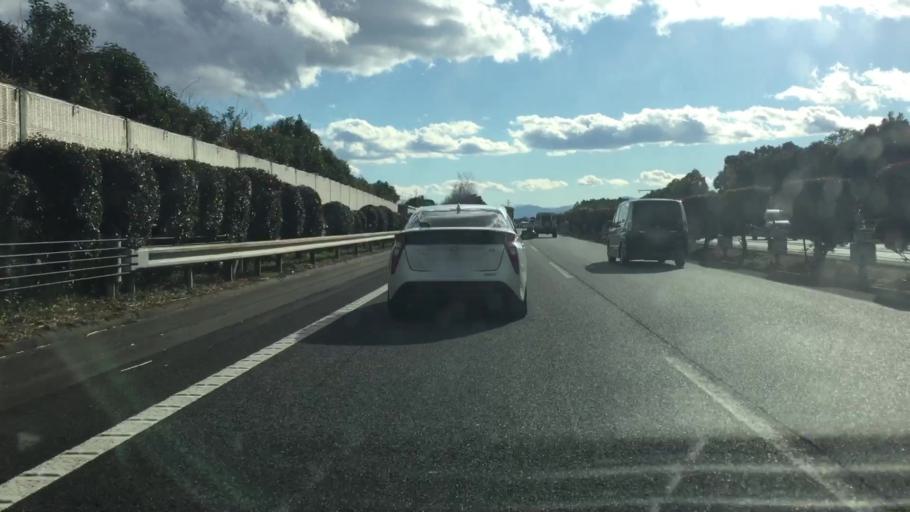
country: JP
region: Gunma
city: Kanekomachi
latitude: 36.4445
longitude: 139.0150
